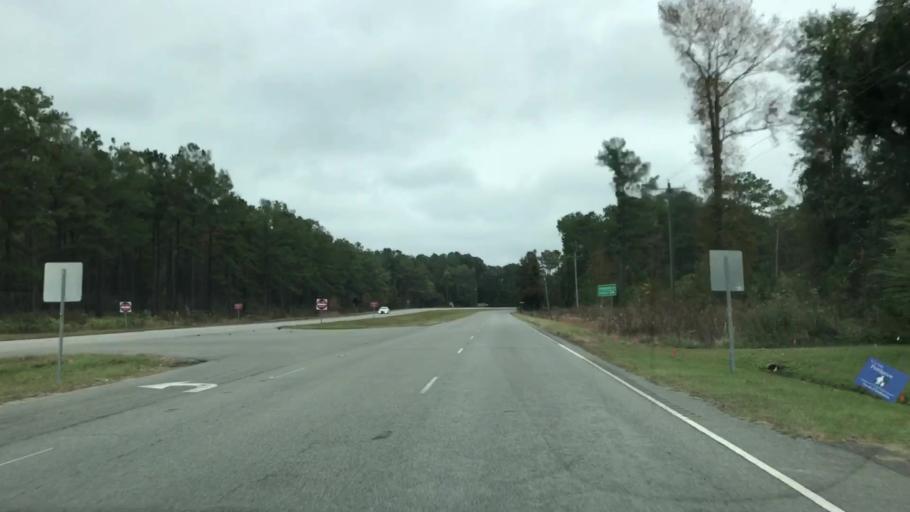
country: US
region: South Carolina
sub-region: Charleston County
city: Awendaw
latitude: 33.0349
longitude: -79.6198
